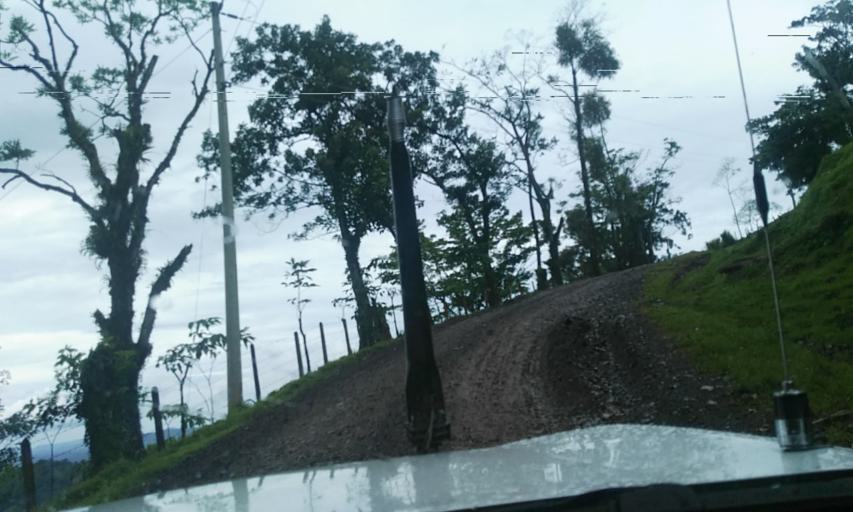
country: NI
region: Matagalpa
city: Rio Blanco
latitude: 13.0187
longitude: -85.2080
